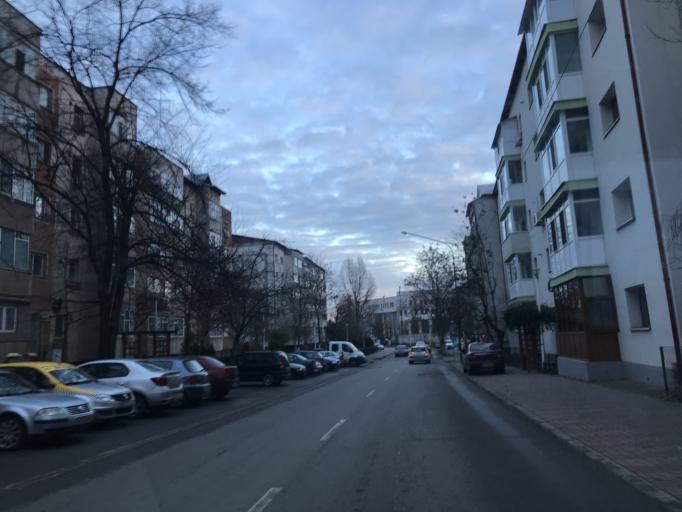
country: RO
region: Olt
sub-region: Municipiul Slatina
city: Slatina
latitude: 44.4256
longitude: 24.3690
